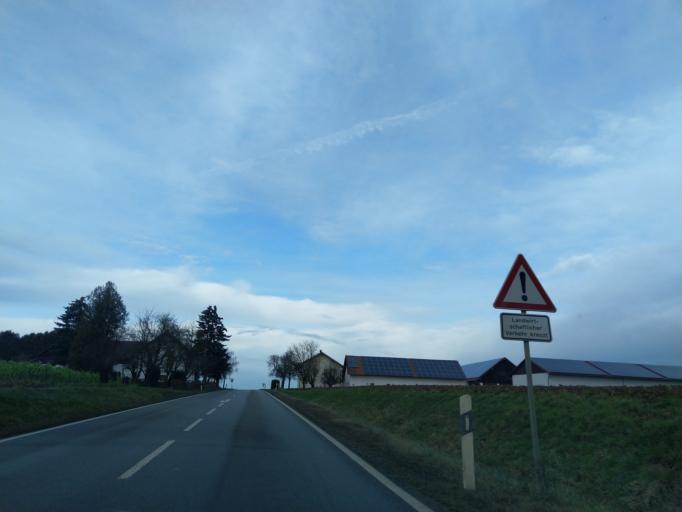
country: DE
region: Bavaria
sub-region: Lower Bavaria
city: Osterhofen
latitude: 48.6658
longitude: 13.0388
